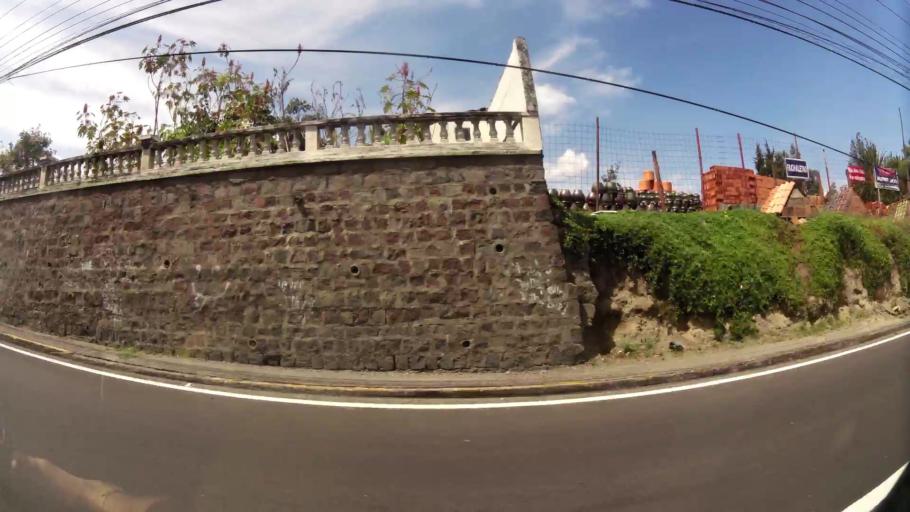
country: EC
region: Pichincha
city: Quito
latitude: -0.2115
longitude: -78.4224
